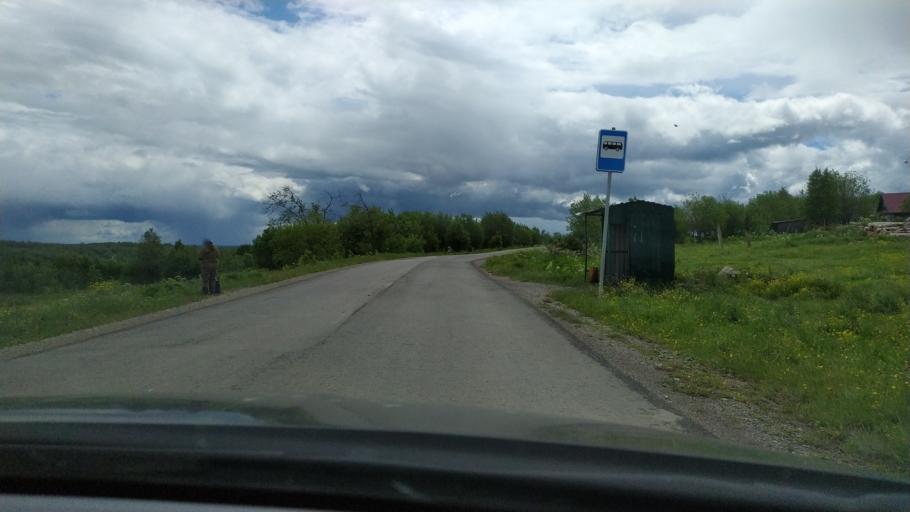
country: RU
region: Perm
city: Gremyachinsk
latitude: 58.5341
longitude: 57.8285
